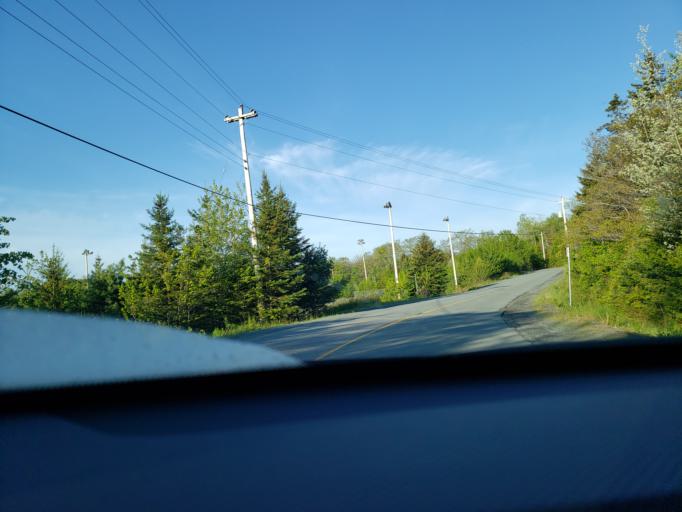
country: CA
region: Nova Scotia
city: Cole Harbour
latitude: 44.7423
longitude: -63.3791
